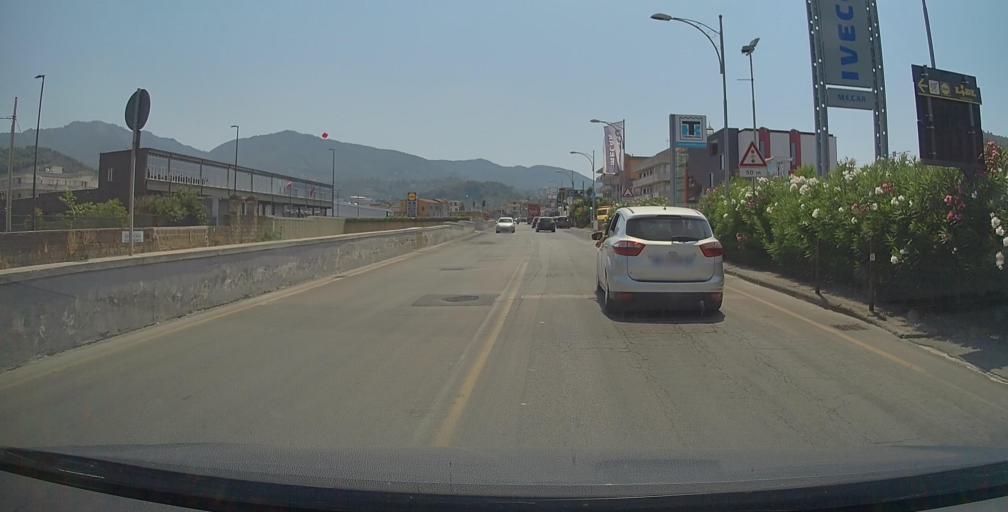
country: IT
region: Campania
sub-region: Provincia di Salerno
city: Nocera Superiore
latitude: 40.7358
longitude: 14.6801
